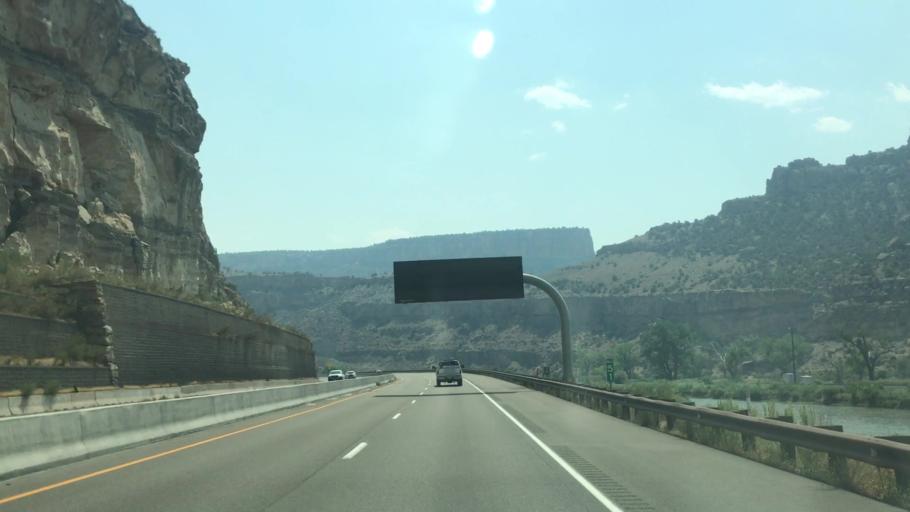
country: US
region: Colorado
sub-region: Mesa County
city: Palisade
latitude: 39.2024
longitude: -108.2664
